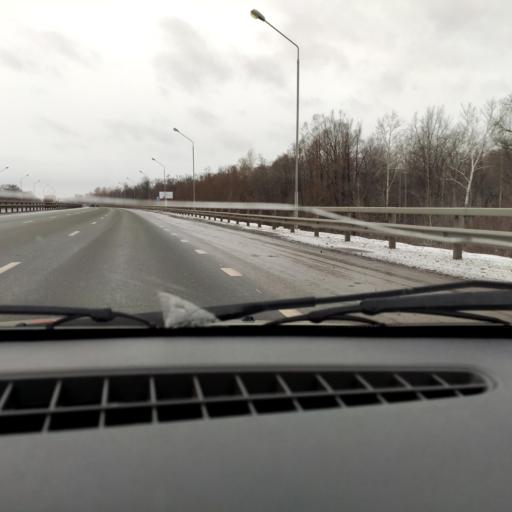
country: RU
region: Bashkortostan
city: Ufa
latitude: 54.6588
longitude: 55.8886
